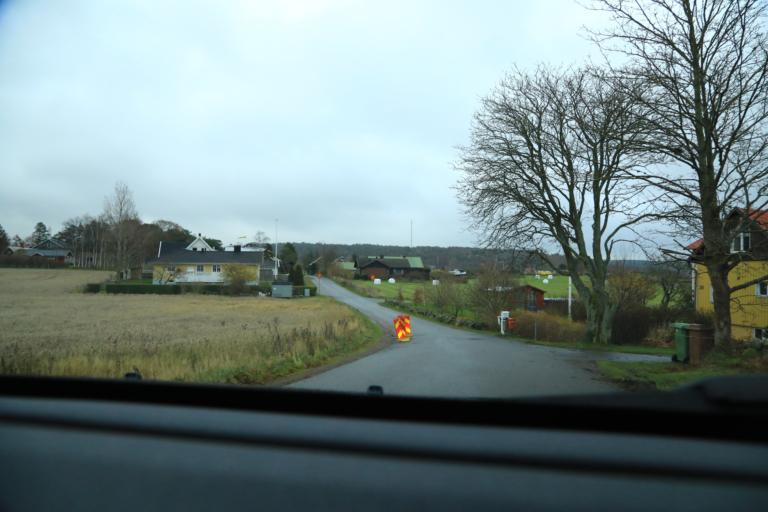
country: SE
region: Halland
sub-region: Varbergs Kommun
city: Varberg
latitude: 57.1715
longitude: 12.2179
